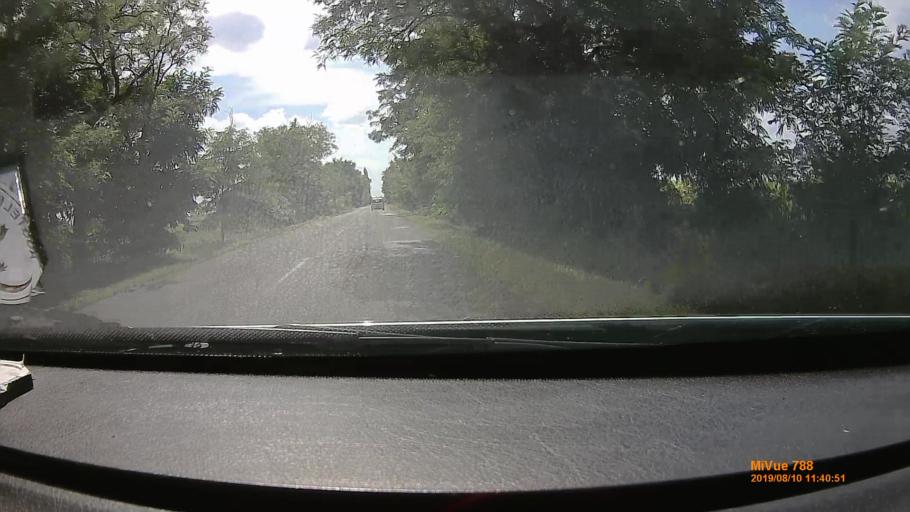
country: HU
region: Borsod-Abauj-Zemplen
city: Szentistvan
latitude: 47.7557
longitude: 20.6051
